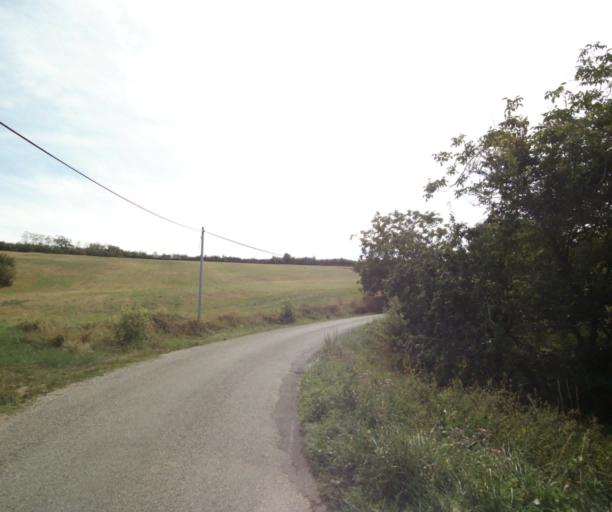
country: FR
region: Midi-Pyrenees
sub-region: Departement de l'Ariege
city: Lezat-sur-Leze
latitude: 43.2424
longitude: 1.4003
